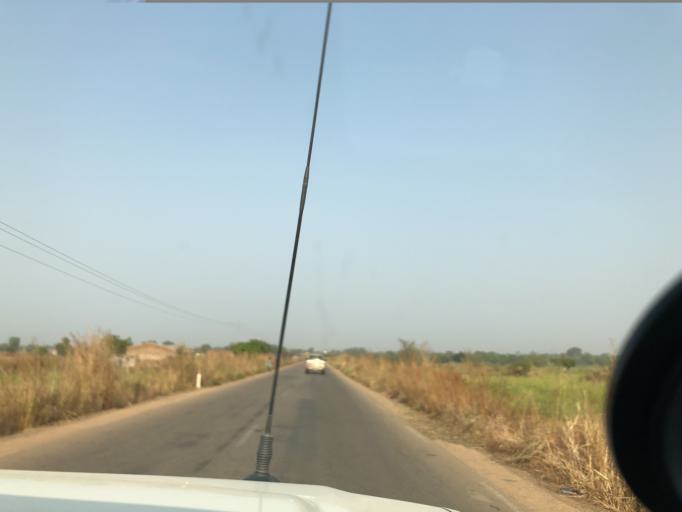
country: TD
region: Logone Occidental
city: Moundou
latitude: 8.5771
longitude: 16.0371
